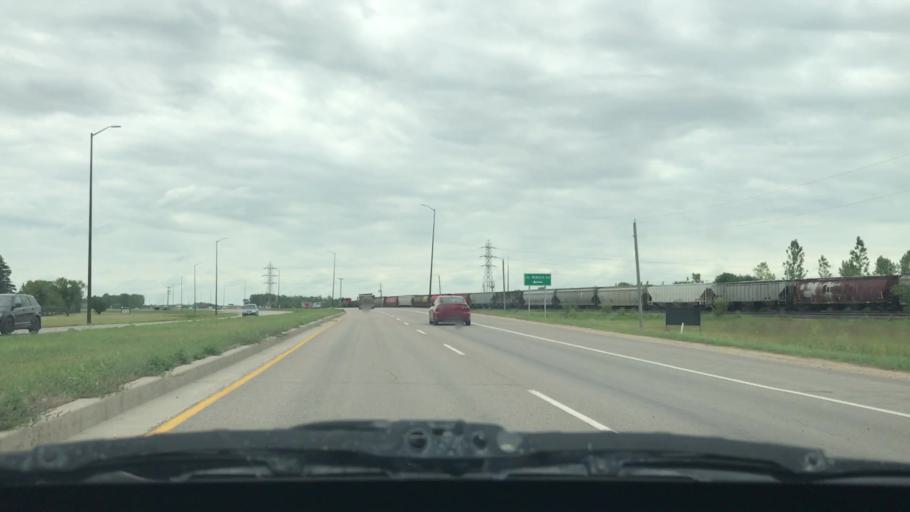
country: CA
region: Manitoba
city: Winnipeg
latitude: 49.8437
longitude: -96.9917
